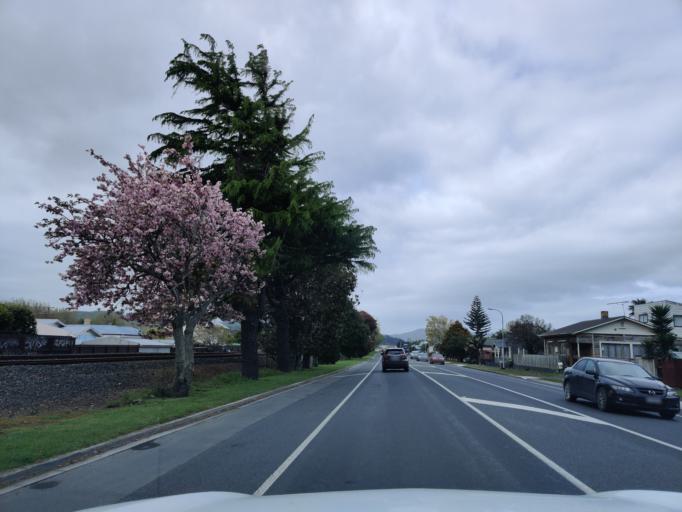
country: NZ
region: Waikato
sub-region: Waikato District
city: Ngaruawahia
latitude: -37.5496
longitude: 175.1586
